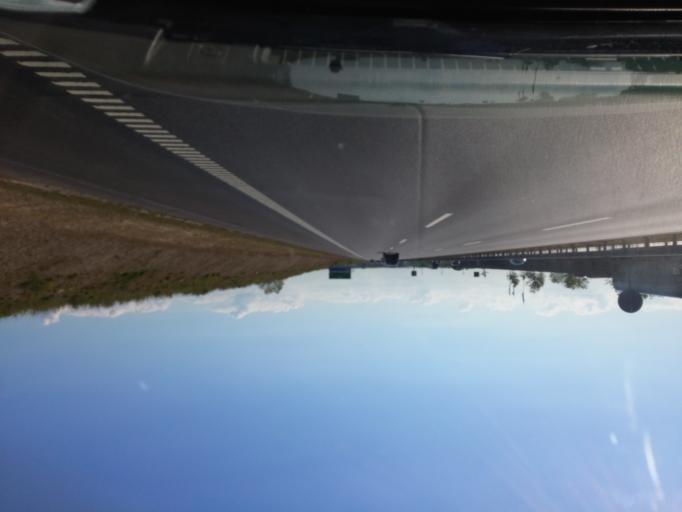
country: DK
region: South Denmark
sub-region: Middelfart Kommune
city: Norre Aby
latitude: 55.4783
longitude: 9.8806
